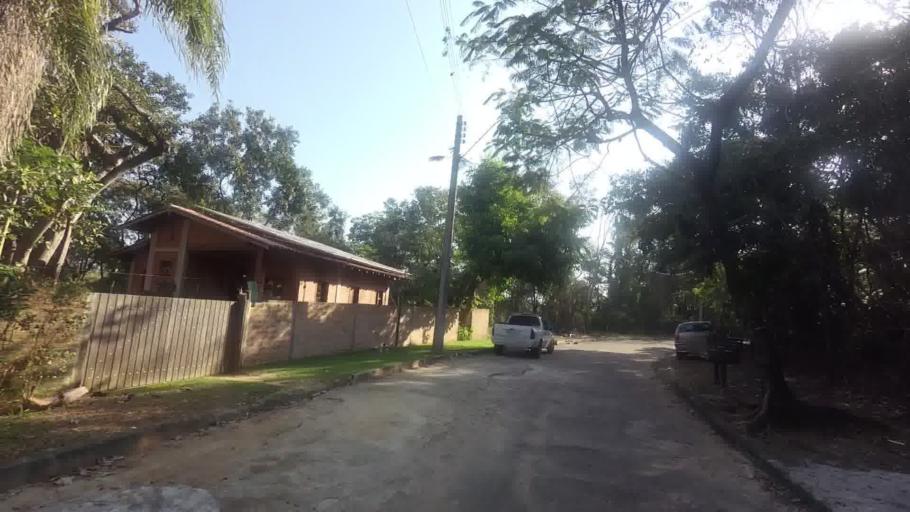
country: BR
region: Espirito Santo
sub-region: Guarapari
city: Guarapari
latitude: -20.7293
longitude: -40.5367
